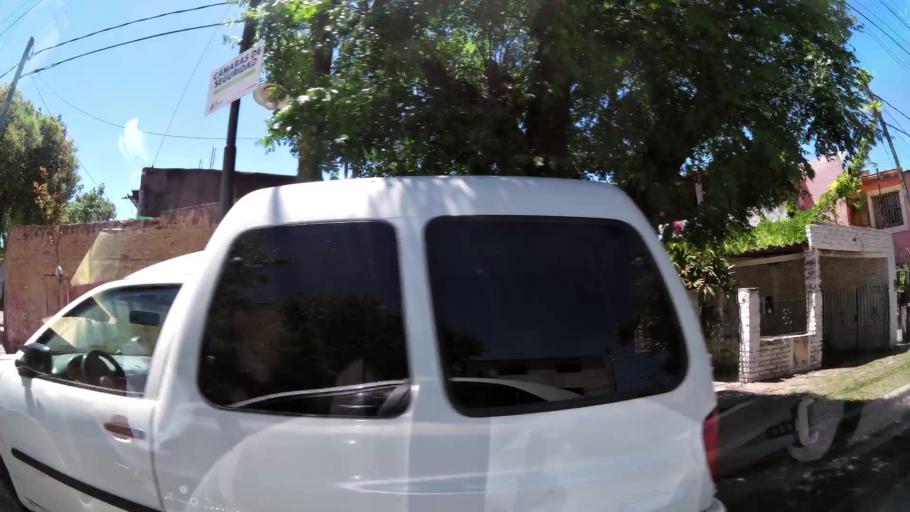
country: AR
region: Buenos Aires
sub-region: Partido de Tigre
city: Tigre
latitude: -34.4496
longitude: -58.5570
